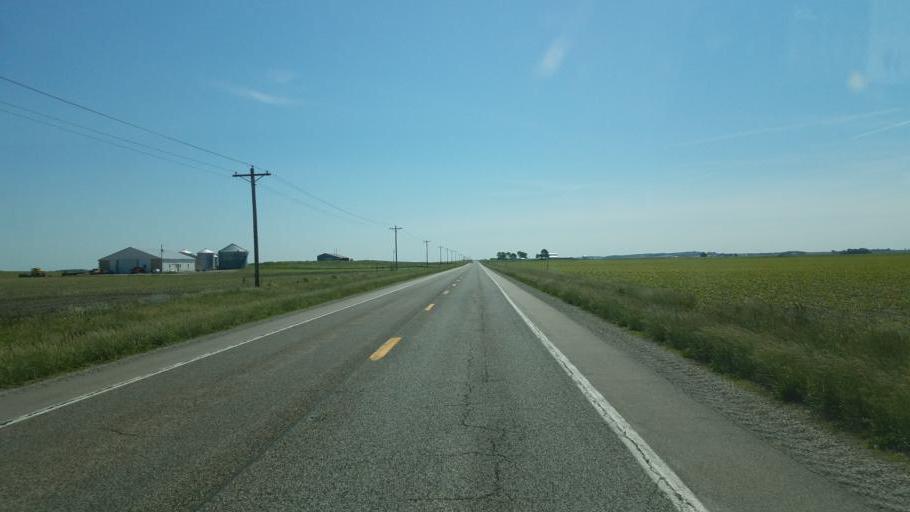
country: US
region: Illinois
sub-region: Mason County
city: Manito
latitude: 40.3037
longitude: -89.7695
